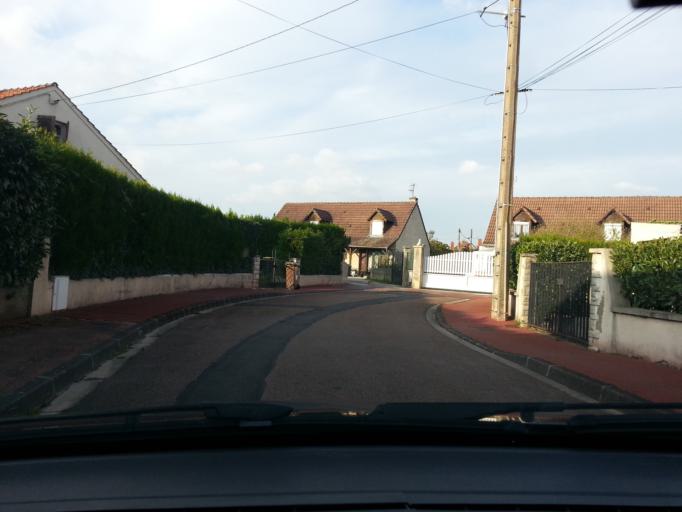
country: FR
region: Bourgogne
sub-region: Departement de Saone-et-Loire
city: Chatenoy-le-Royal
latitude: 46.7794
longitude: 4.8204
